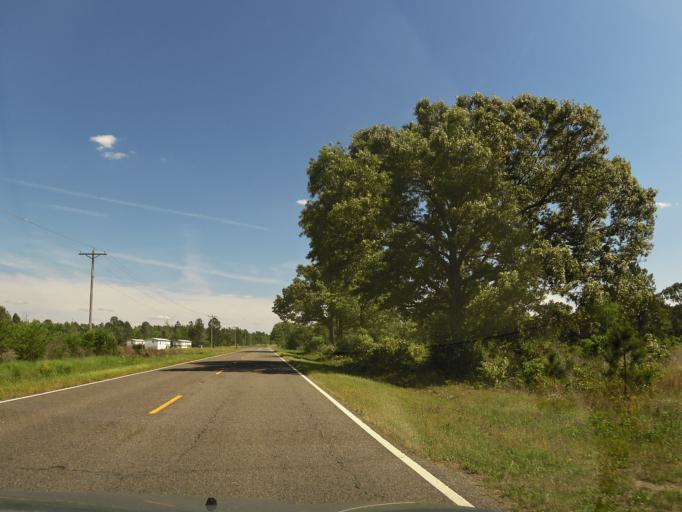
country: US
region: South Carolina
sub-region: Barnwell County
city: Williston
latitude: 33.4589
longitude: -81.4974
